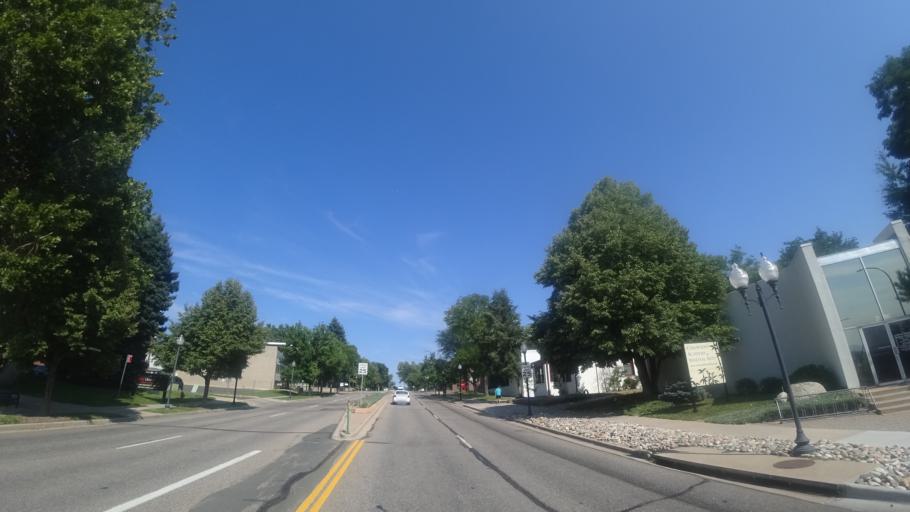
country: US
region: Colorado
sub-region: Arapahoe County
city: Littleton
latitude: 39.6132
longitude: -105.0127
